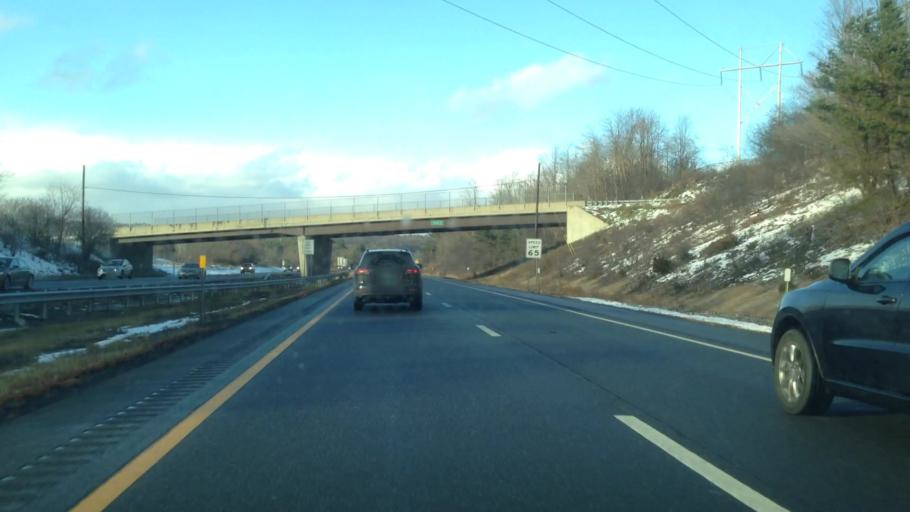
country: US
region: New York
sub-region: Schenectady County
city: Rotterdam
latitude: 42.8050
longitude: -74.0183
